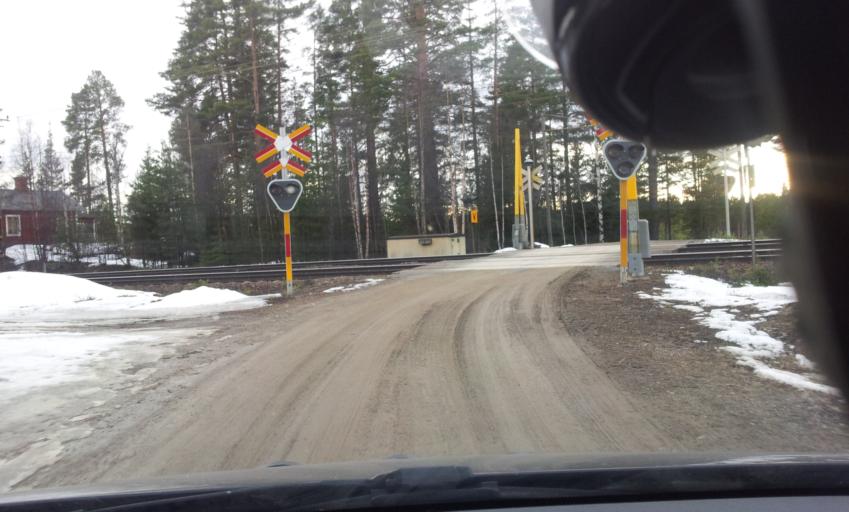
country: SE
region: Vaesternorrland
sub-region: Ange Kommun
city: Ange
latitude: 62.1879
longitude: 15.6704
